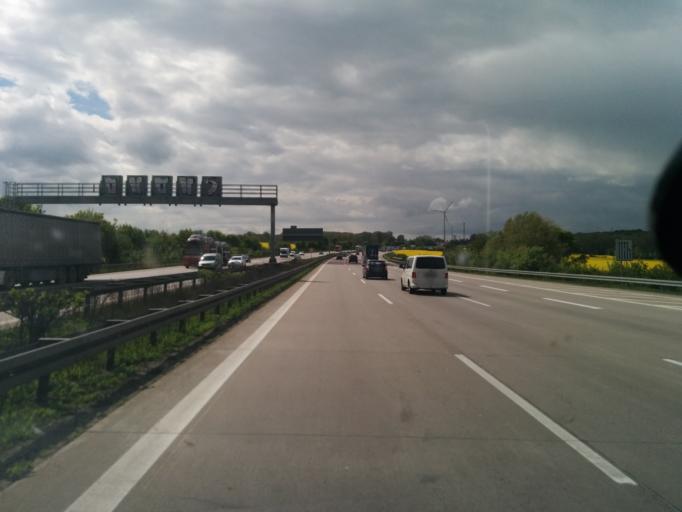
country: DE
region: Saxony-Anhalt
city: Hohenwarsleben
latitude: 52.1655
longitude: 11.5257
